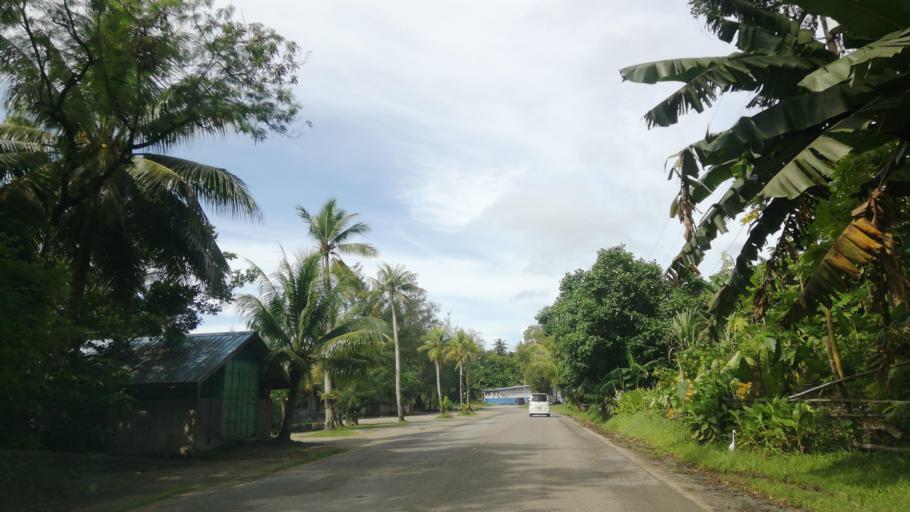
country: FM
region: Yap
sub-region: Weloy Municipality
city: Colonia
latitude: 9.5164
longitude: 138.1202
